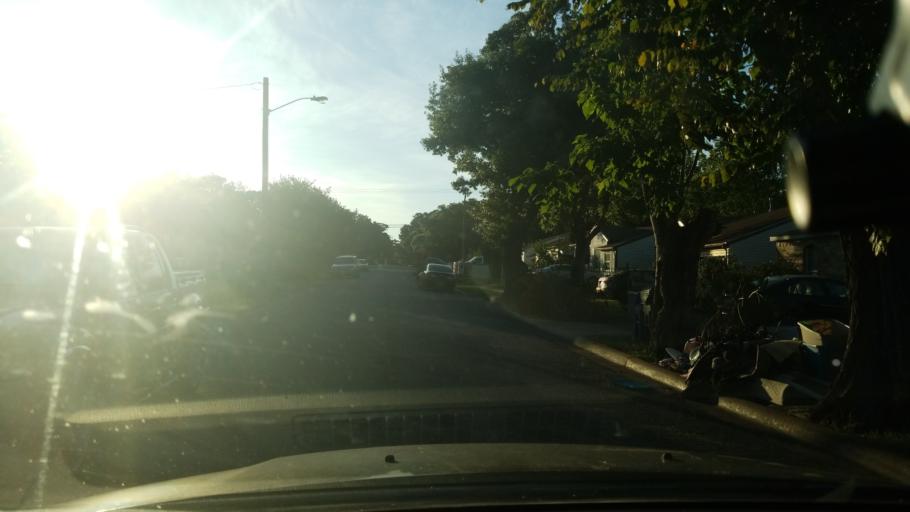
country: US
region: Texas
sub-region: Dallas County
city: Cockrell Hill
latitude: 32.7151
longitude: -96.8276
